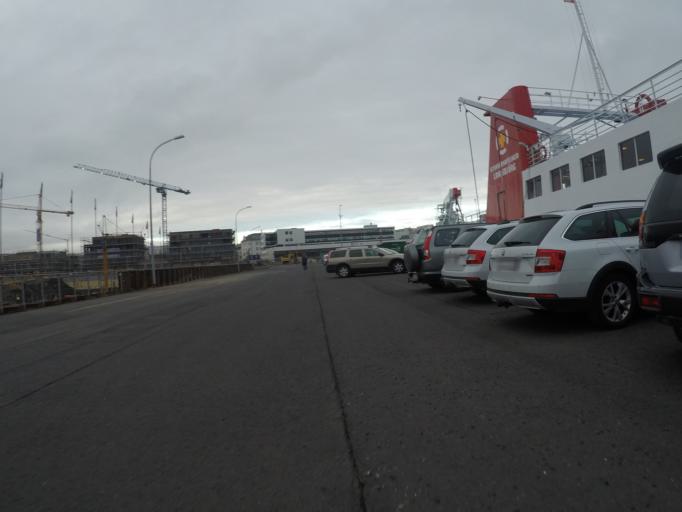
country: IS
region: Capital Region
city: Reykjavik
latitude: 64.1502
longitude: -21.9355
